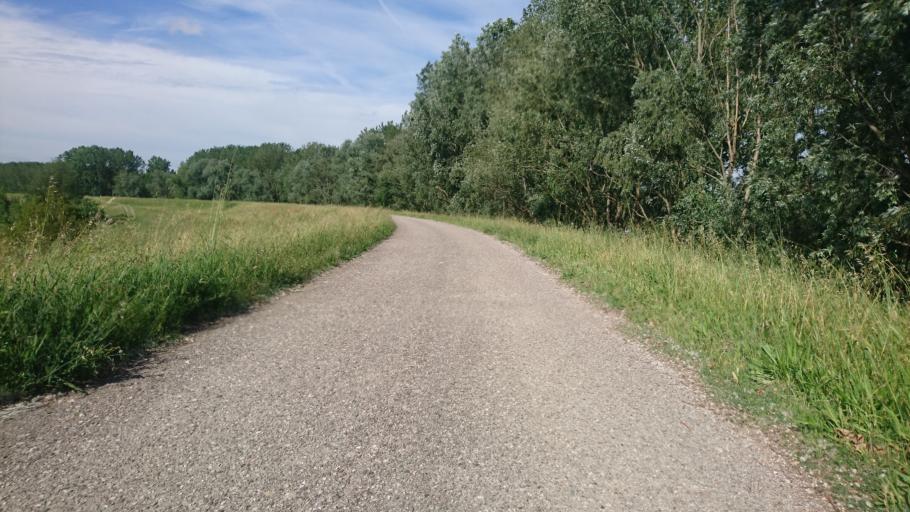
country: IT
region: Veneto
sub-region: Provincia di Rovigo
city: Bergantino
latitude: 45.0506
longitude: 11.2569
